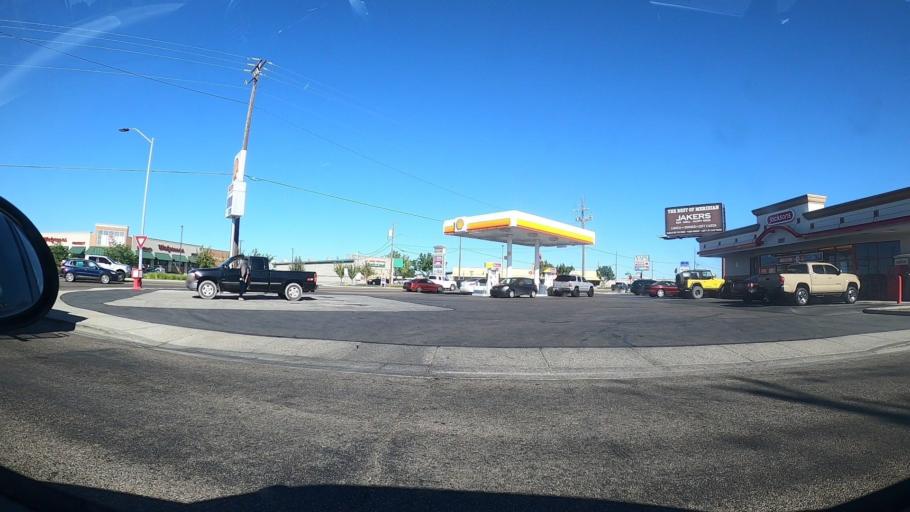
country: US
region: Idaho
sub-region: Canyon County
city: Nampa
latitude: 43.5971
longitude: -116.5930
